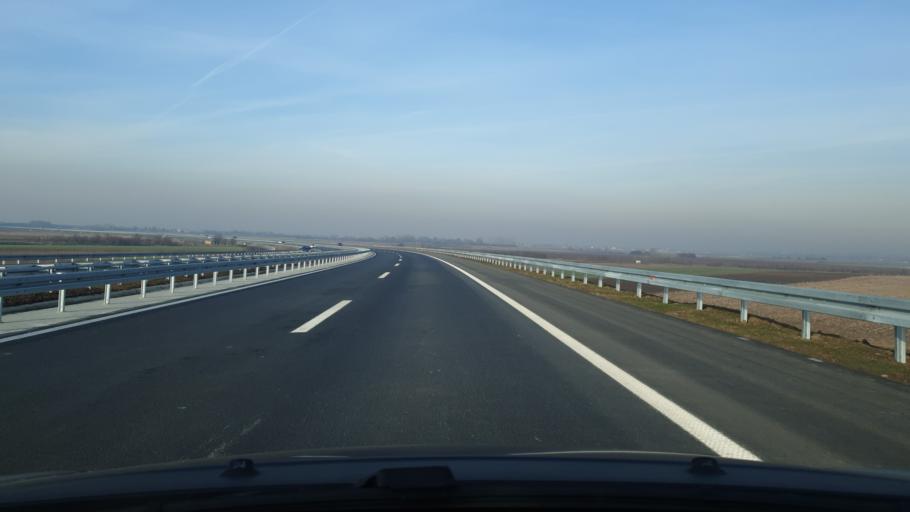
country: RS
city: Boljevci
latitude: 44.7194
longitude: 20.2582
